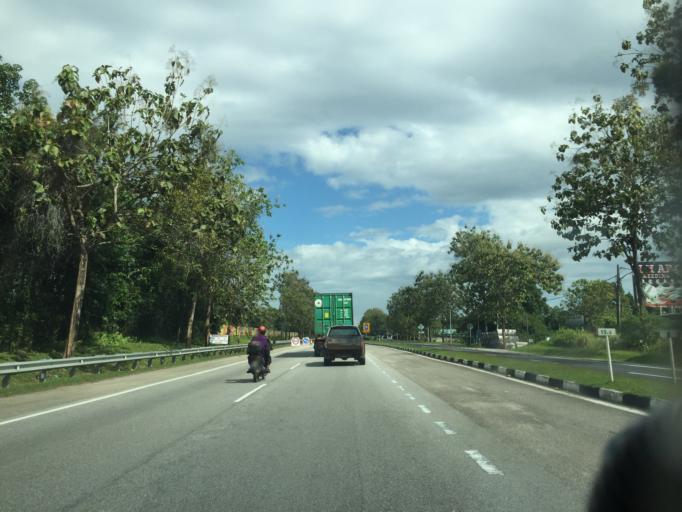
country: MY
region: Kedah
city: Jitra
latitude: 6.3436
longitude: 100.4207
